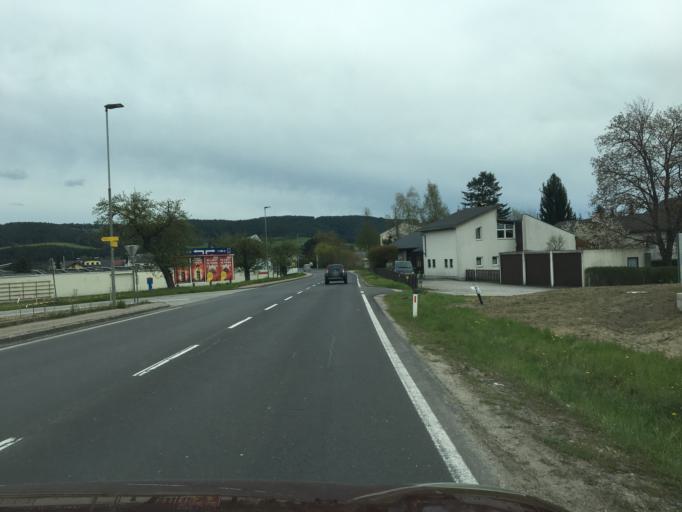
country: AT
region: Upper Austria
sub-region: Politischer Bezirk Freistadt
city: Freistadt
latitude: 48.4999
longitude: 14.4952
